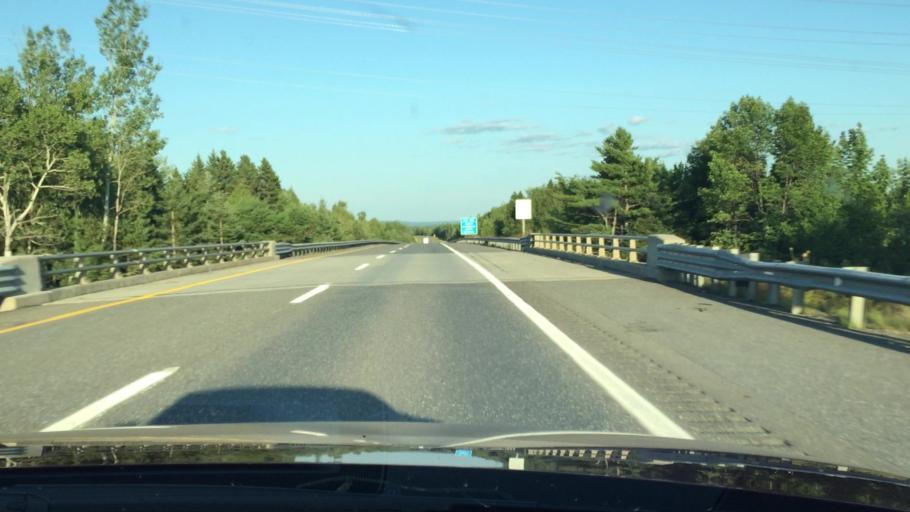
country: US
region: Maine
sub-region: Aroostook County
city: Hodgdon
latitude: 46.1430
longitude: -68.0409
